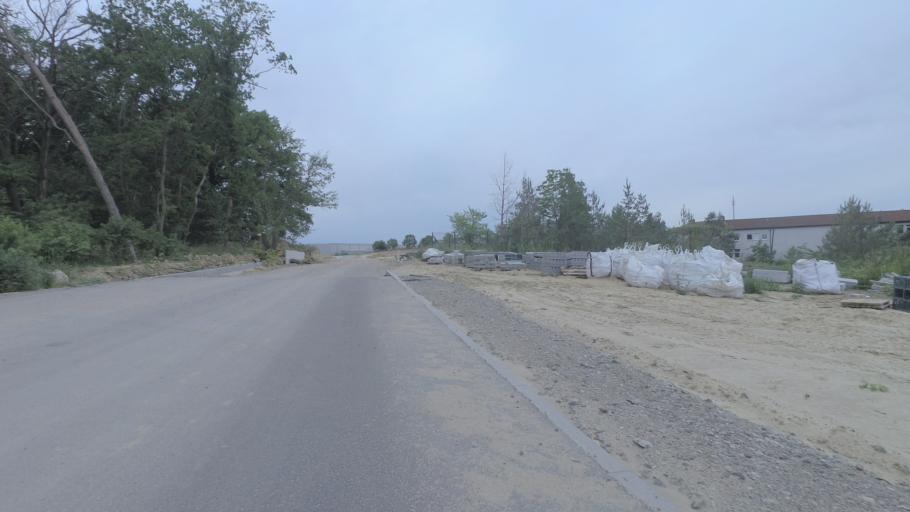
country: DE
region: Brandenburg
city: Rangsdorf
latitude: 52.2993
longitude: 13.4636
